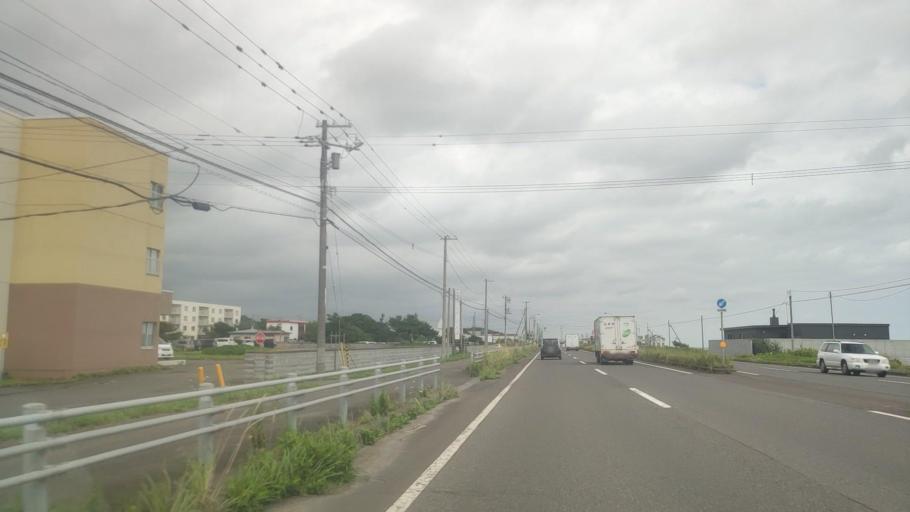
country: JP
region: Hokkaido
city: Shiraoi
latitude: 42.4710
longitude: 141.2311
